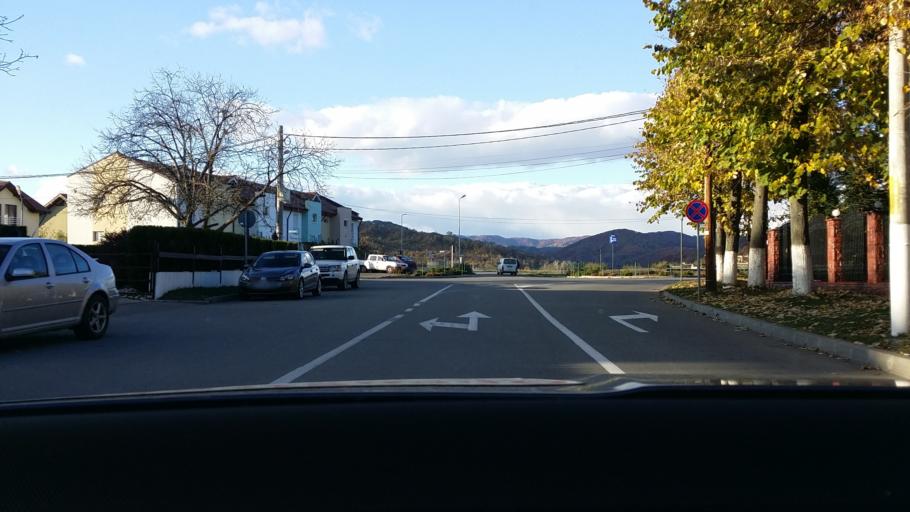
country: RO
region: Prahova
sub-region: Municipiul Campina
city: Campina
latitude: 45.1439
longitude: 25.7330
